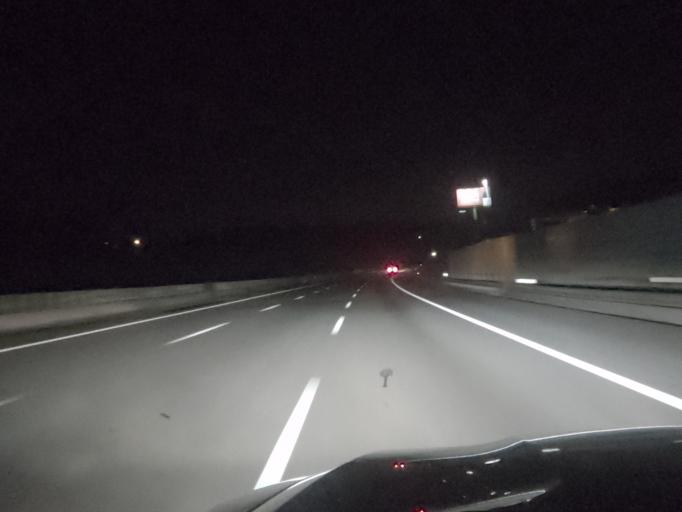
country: PT
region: Aveiro
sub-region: Santa Maria da Feira
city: Feira
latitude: 40.8916
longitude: -8.5682
